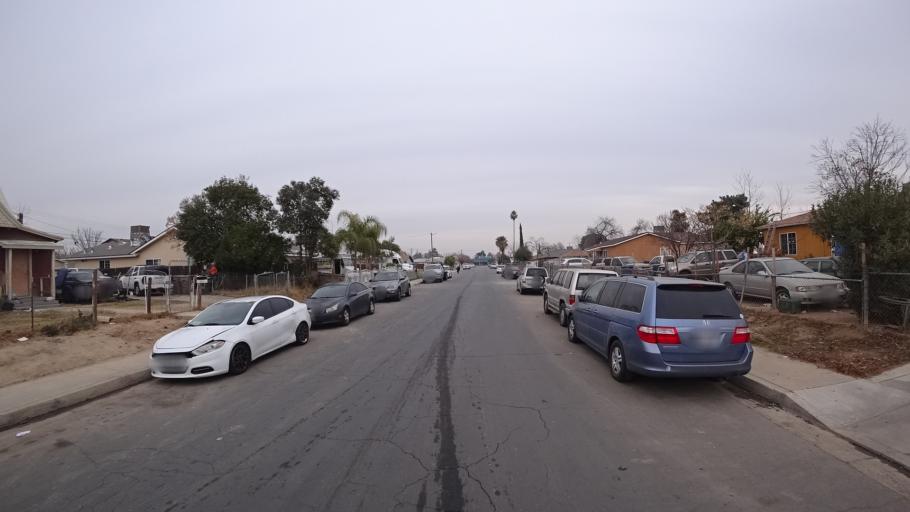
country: US
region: California
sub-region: Kern County
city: Bakersfield
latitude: 35.3657
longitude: -118.9884
